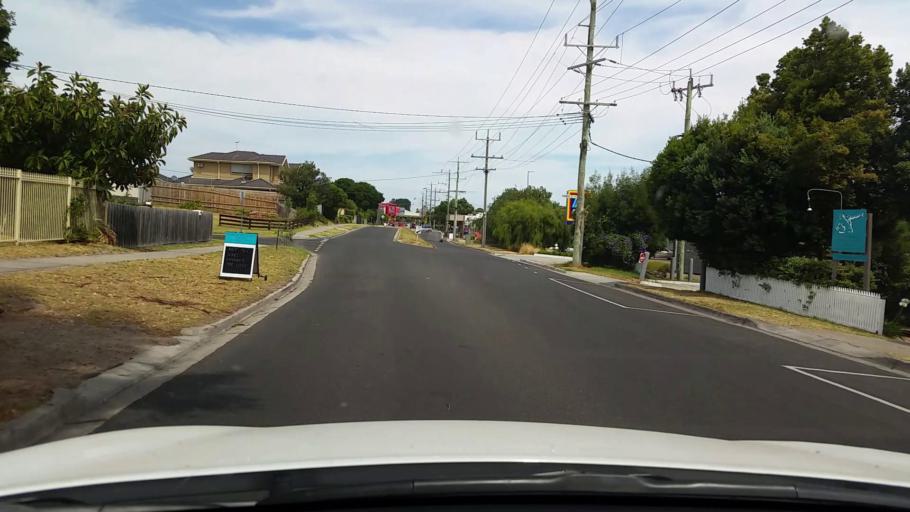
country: AU
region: Victoria
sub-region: Mornington Peninsula
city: Rosebud
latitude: -38.3599
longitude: 144.8949
